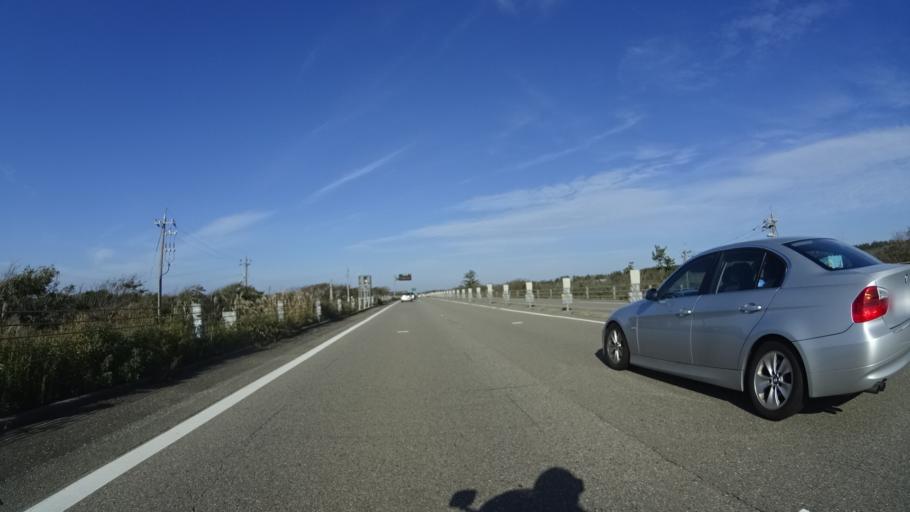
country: JP
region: Ishikawa
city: Hakui
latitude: 36.8081
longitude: 136.7372
